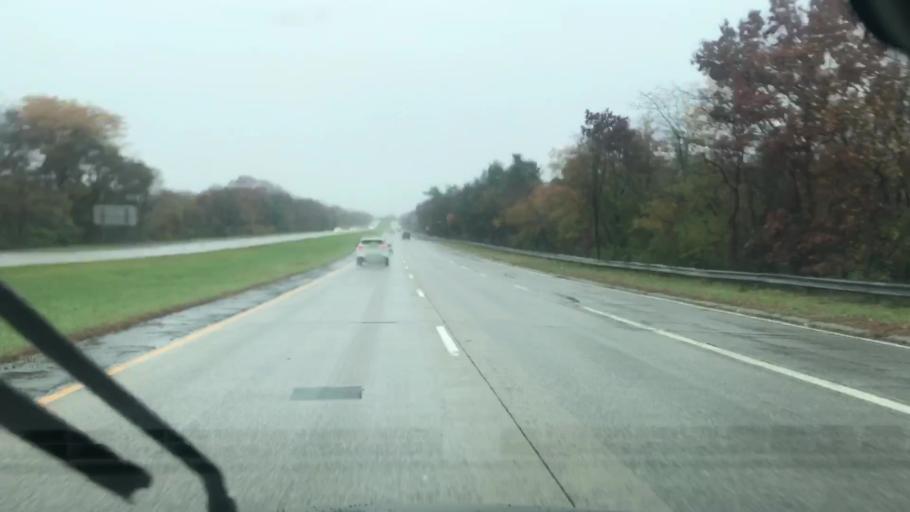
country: US
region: New York
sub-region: Suffolk County
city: North Babylon
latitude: 40.7160
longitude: -73.3143
